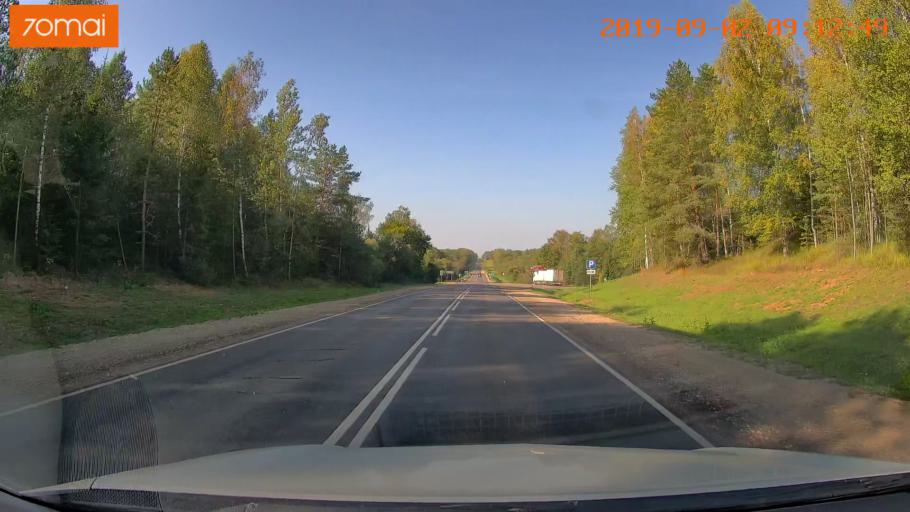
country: RU
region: Kaluga
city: Nikola-Lenivets
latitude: 54.8583
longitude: 35.5494
